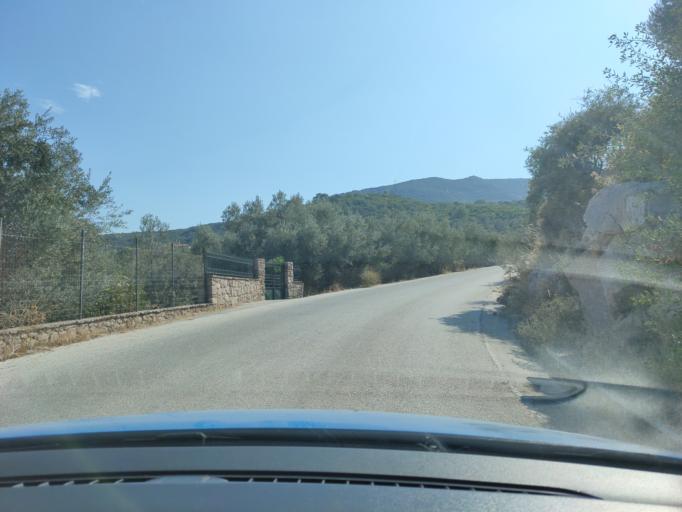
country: GR
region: North Aegean
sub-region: Nomos Lesvou
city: Mantamados
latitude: 39.3741
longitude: 26.3092
